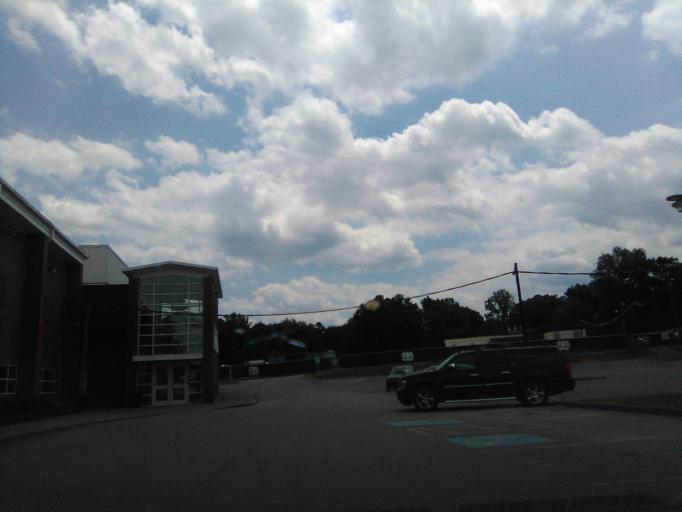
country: US
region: Tennessee
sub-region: Davidson County
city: Belle Meade
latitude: 36.1280
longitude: -86.8378
